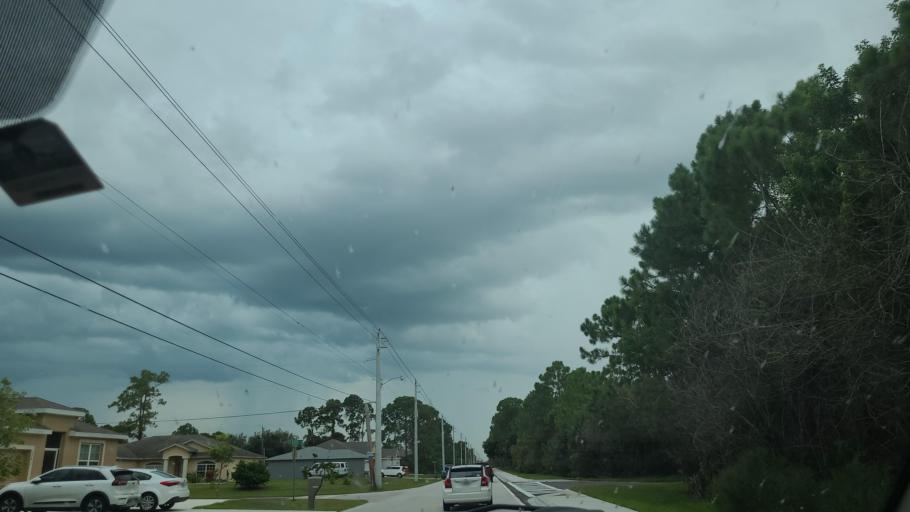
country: US
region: Florida
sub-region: Saint Lucie County
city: Port Saint Lucie
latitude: 27.2329
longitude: -80.3997
